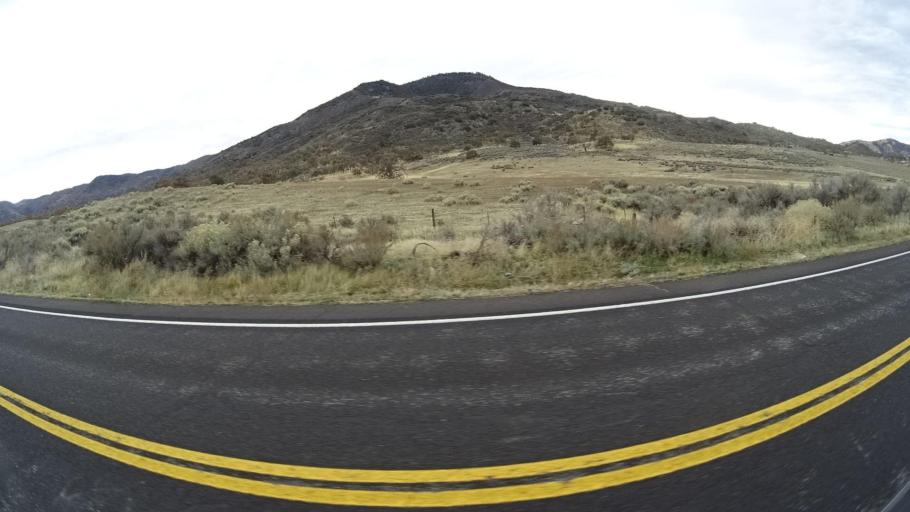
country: US
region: California
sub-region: Kern County
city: Stallion Springs
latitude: 35.0950
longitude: -118.5897
